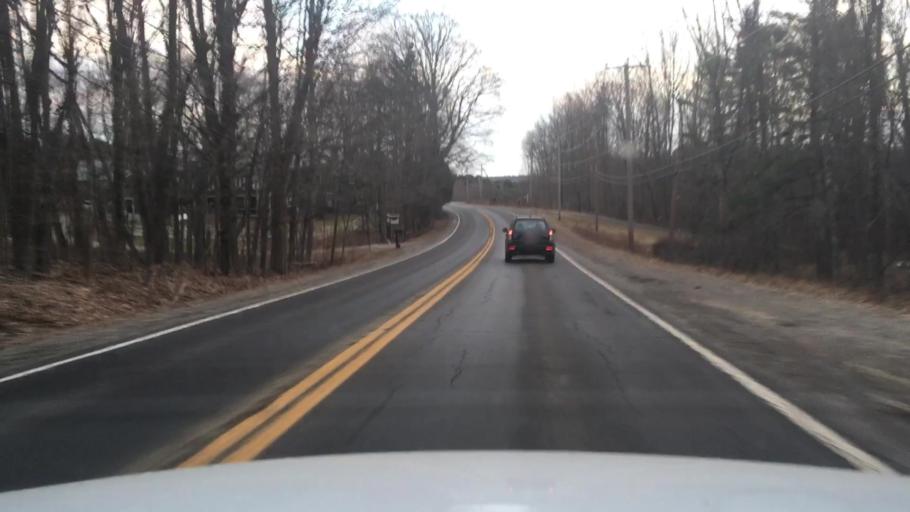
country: US
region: Maine
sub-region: Lincoln County
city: Damariscotta
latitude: 44.0052
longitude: -69.5302
